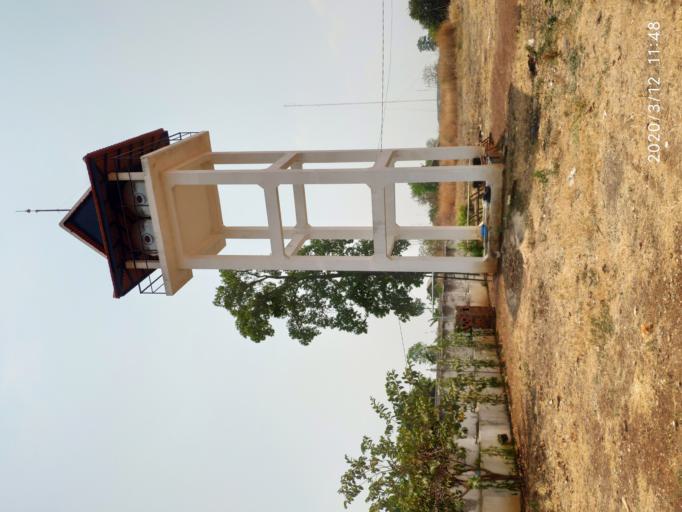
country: KH
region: Preah Vihear
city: Tbeng Meanchey
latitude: 13.7169
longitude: 104.5456
